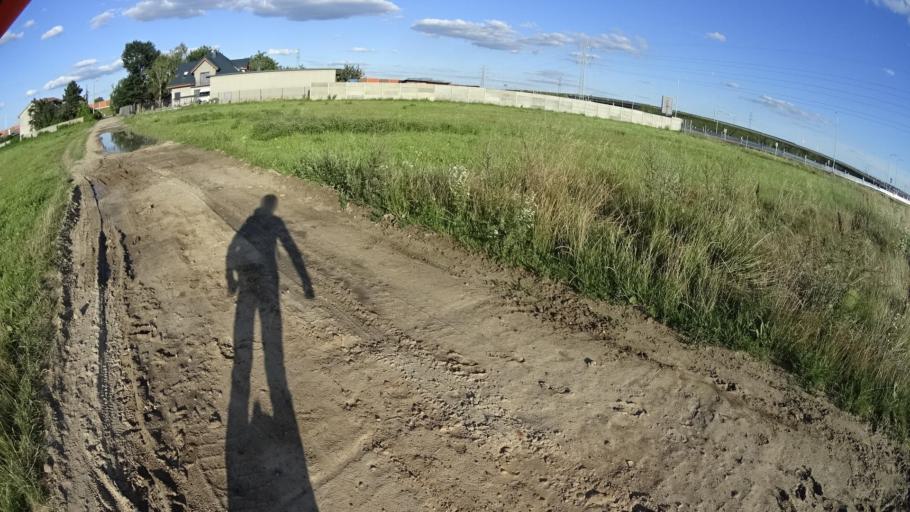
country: PL
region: Masovian Voivodeship
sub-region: Powiat piaseczynski
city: Lesznowola
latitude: 52.0910
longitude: 20.9671
